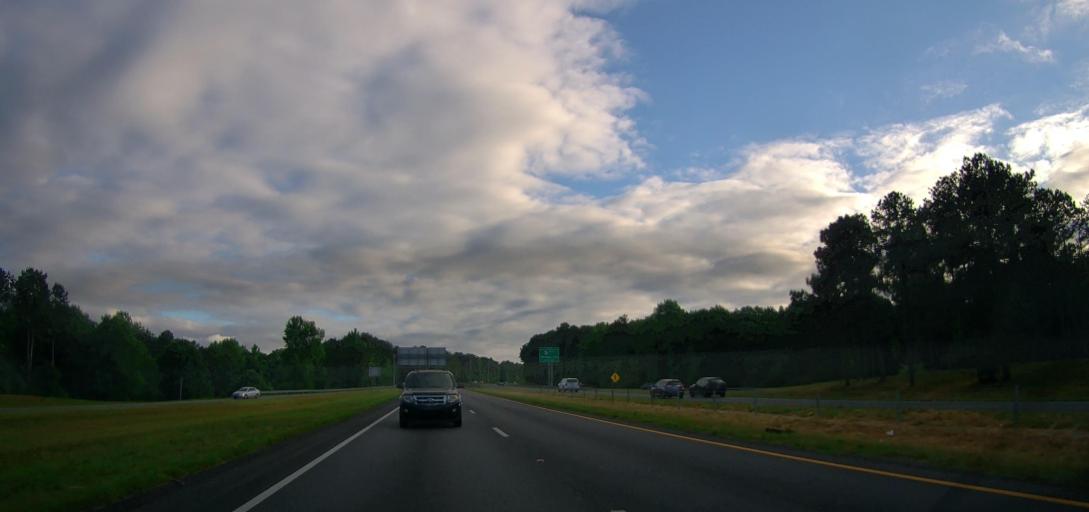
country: US
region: Georgia
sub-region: Clarke County
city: Athens
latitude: 33.9309
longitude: -83.3681
